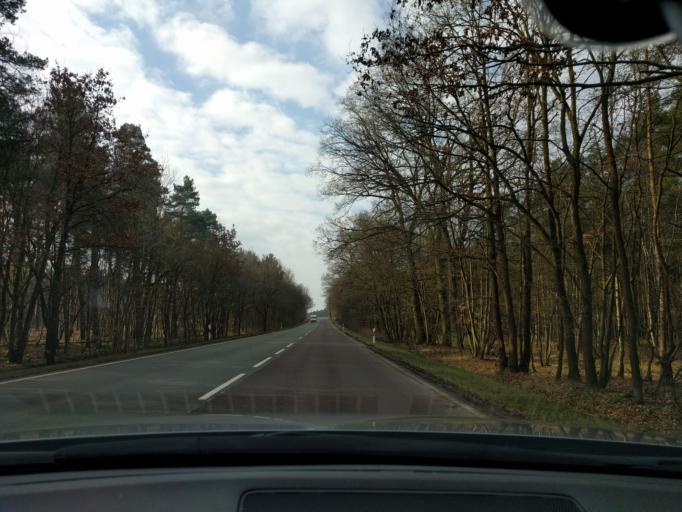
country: DE
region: Saxony-Anhalt
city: Colbitz
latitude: 52.3736
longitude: 11.6181
